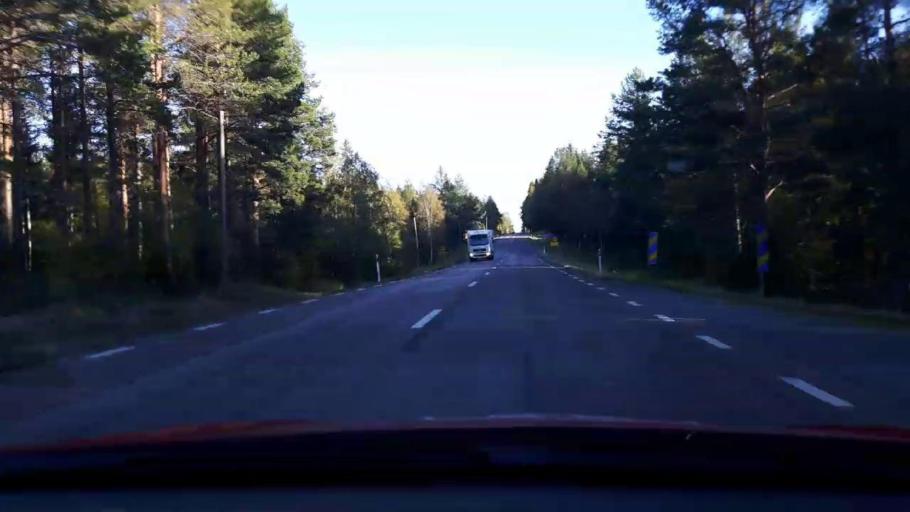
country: SE
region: Jaemtland
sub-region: OEstersunds Kommun
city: Brunflo
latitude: 63.0613
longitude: 14.8513
